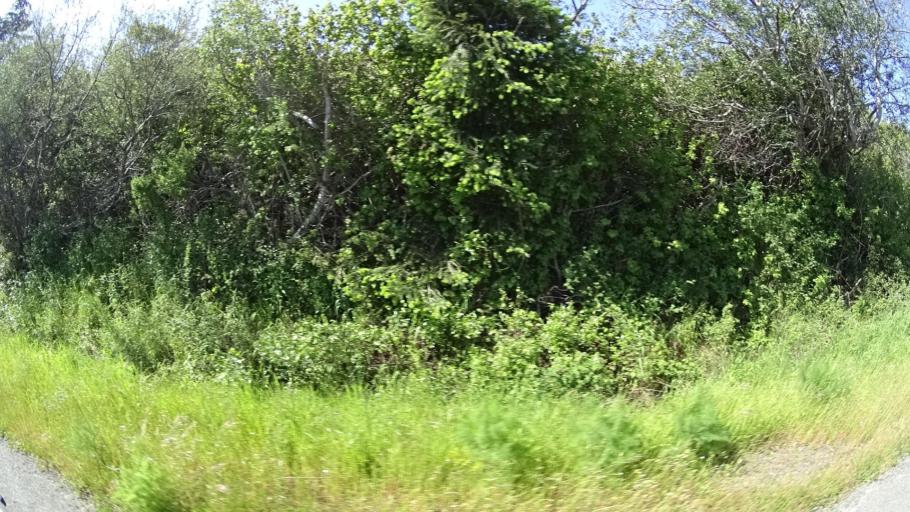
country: US
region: California
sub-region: Humboldt County
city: Ferndale
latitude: 40.3282
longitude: -124.2990
